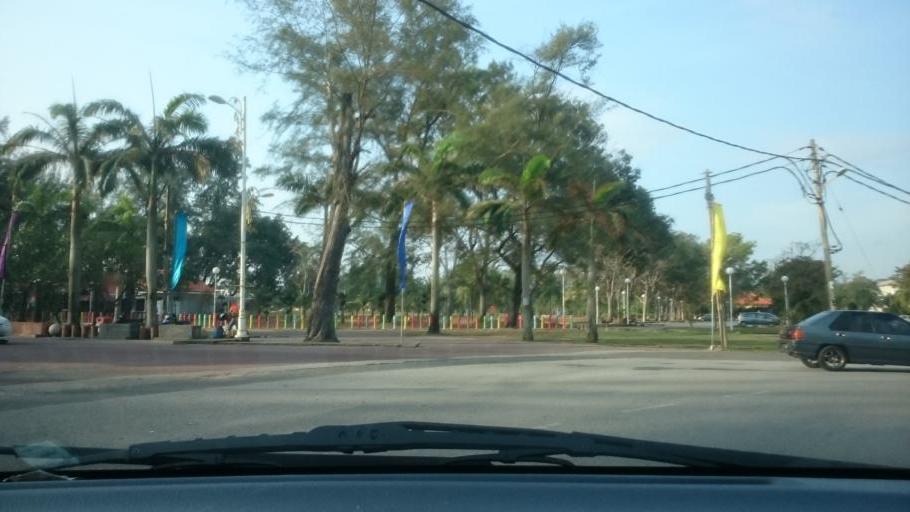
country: MY
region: Terengganu
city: Kuala Terengganu
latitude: 5.3242
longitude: 103.1539
